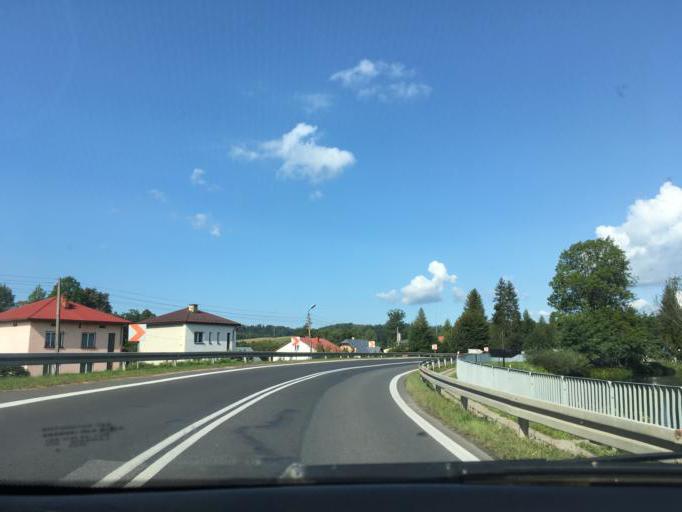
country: PL
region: Subcarpathian Voivodeship
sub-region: Powiat leski
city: Olszanica
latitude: 49.4749
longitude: 22.4480
